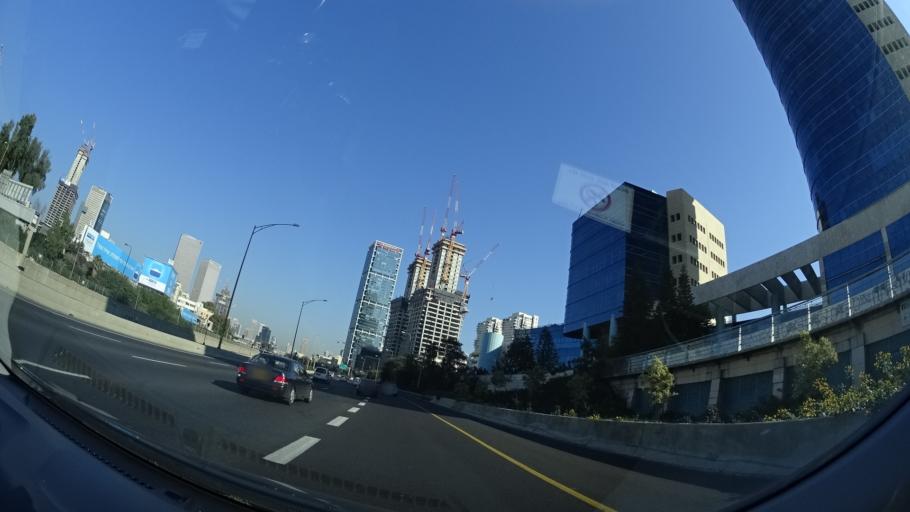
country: IL
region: Tel Aviv
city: Tel Aviv
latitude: 32.0655
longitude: 34.7913
